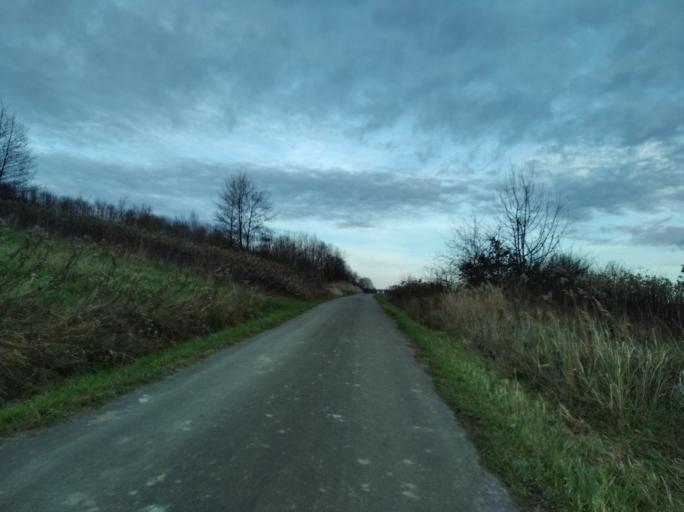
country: PL
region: Subcarpathian Voivodeship
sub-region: Powiat brzozowski
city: Domaradz
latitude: 49.7827
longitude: 21.9358
